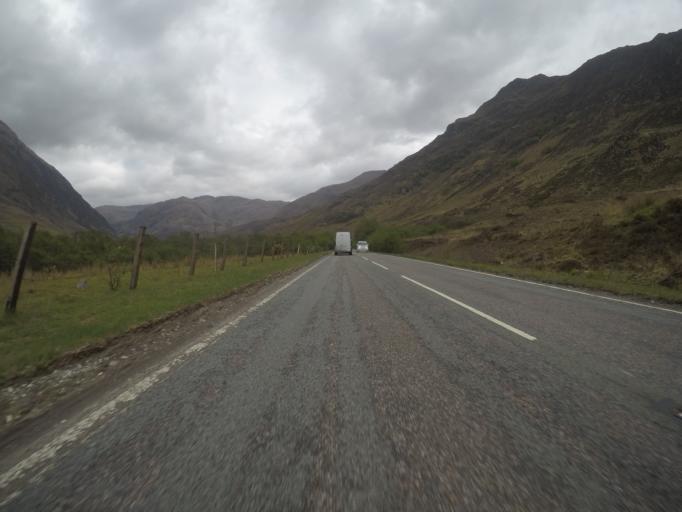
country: GB
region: Scotland
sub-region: Highland
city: Fort William
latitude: 57.1865
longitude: -5.3831
